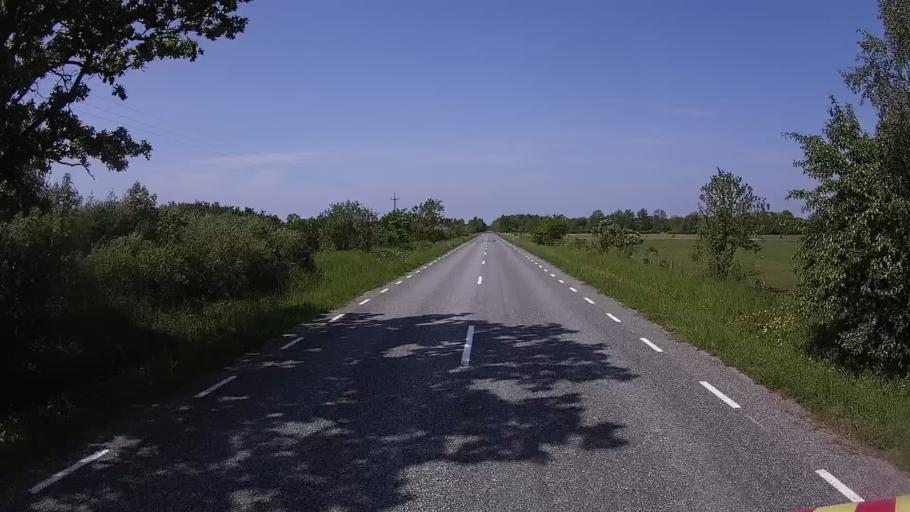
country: EE
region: Saare
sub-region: Kuressaare linn
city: Kuressaare
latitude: 58.3675
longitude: 22.0510
